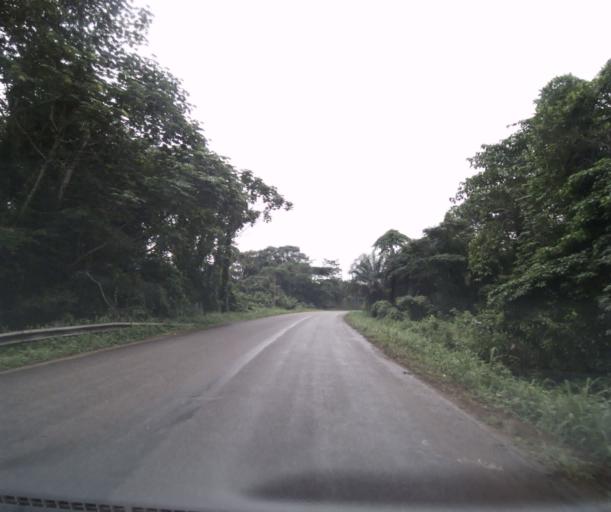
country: CM
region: Littoral
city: Edea
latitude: 3.8372
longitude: 10.4626
